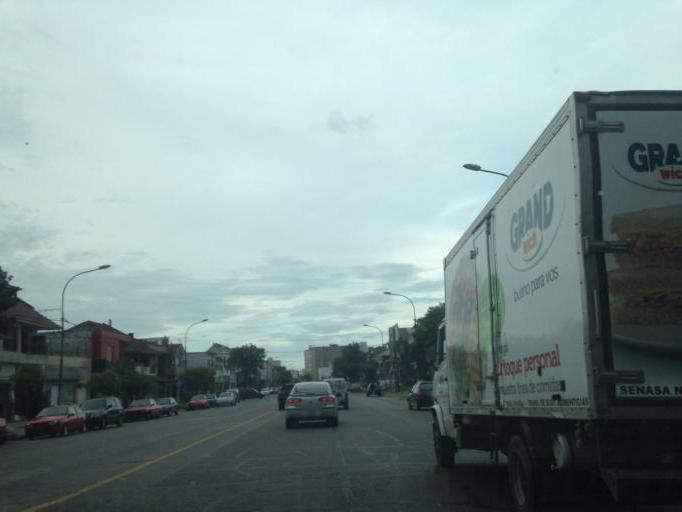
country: AR
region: Buenos Aires
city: Mar del Plata
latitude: -38.0231
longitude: -57.5761
